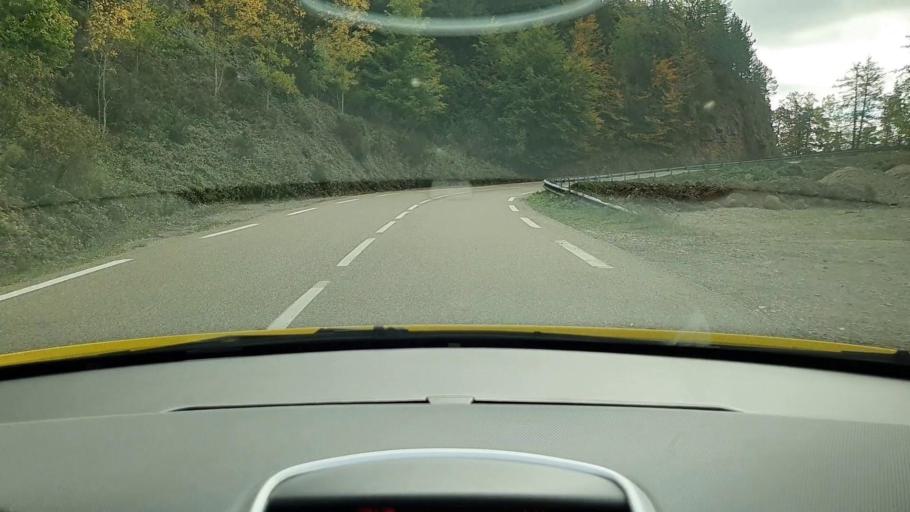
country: FR
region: Languedoc-Roussillon
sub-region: Departement de la Lozere
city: Meyrueis
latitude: 44.1245
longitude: 3.4482
